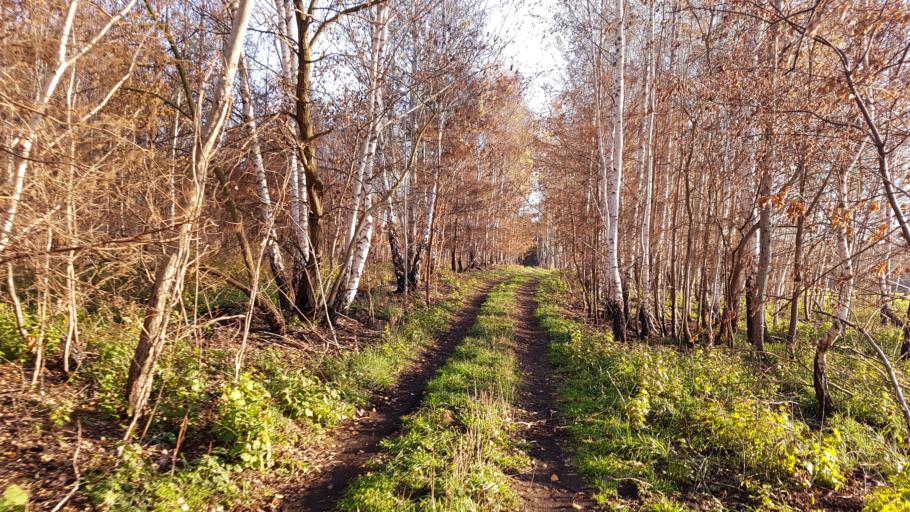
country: DE
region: Brandenburg
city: Schilda
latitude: 51.5917
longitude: 13.4026
